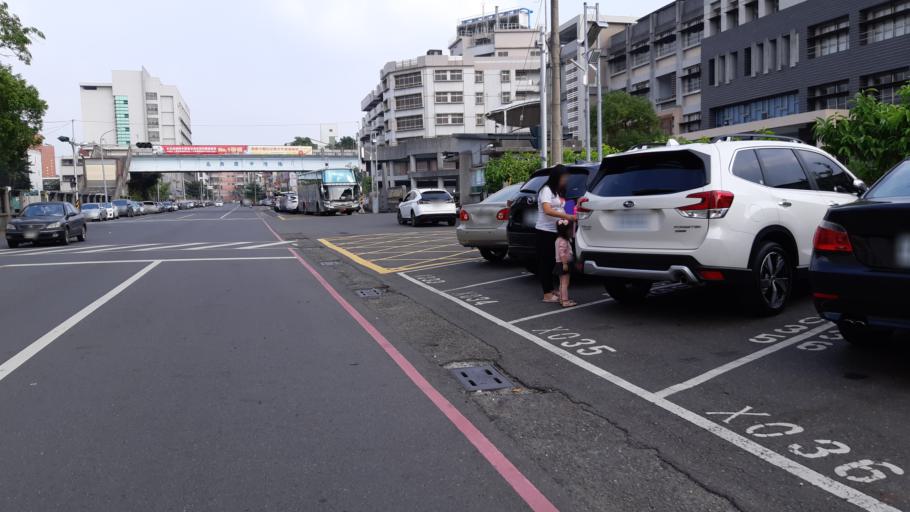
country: TW
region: Taiwan
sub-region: Chiayi
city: Jiayi Shi
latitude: 23.4686
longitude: 120.4617
